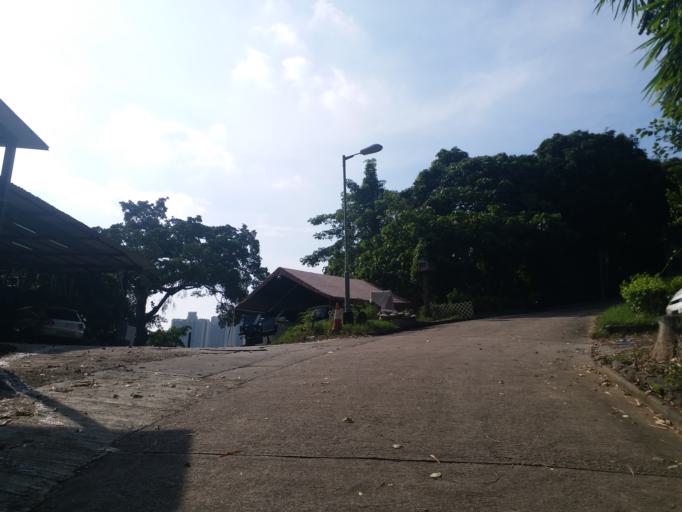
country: HK
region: Yuen Long
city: Yuen Long Kau Hui
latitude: 22.4443
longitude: 114.0098
